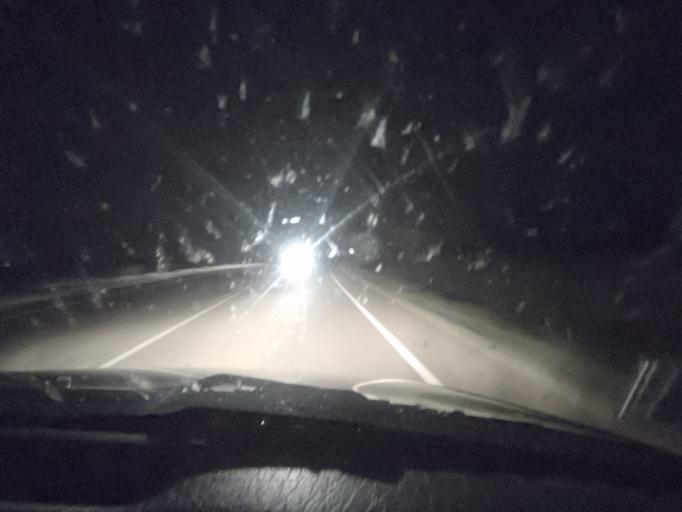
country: ES
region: Castille and Leon
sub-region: Provincia de Salamanca
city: Robleda
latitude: 40.3953
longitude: -6.6067
